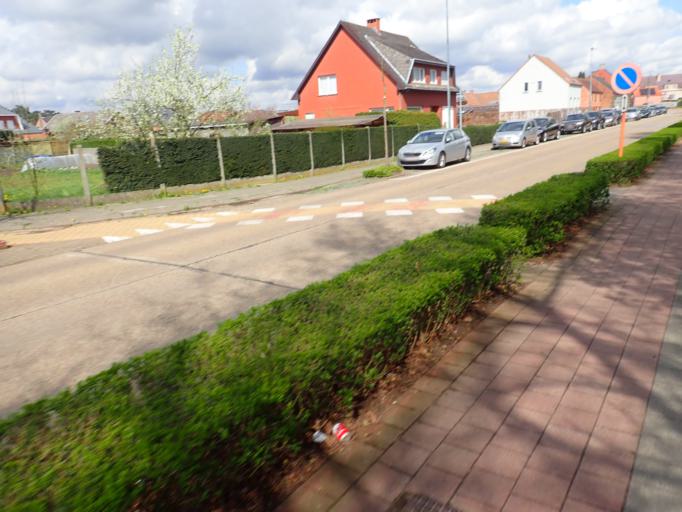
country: BE
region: Flanders
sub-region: Provincie Antwerpen
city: Vorselaar
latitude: 51.1995
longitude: 4.7680
